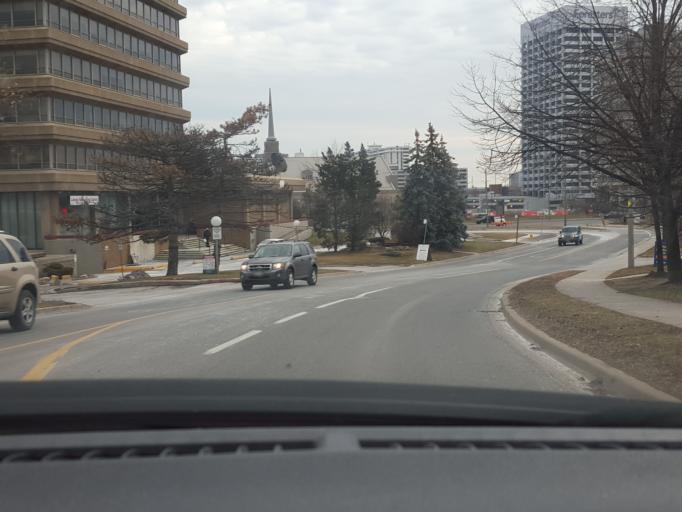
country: CA
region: Ontario
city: Willowdale
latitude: 43.7229
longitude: -79.3364
